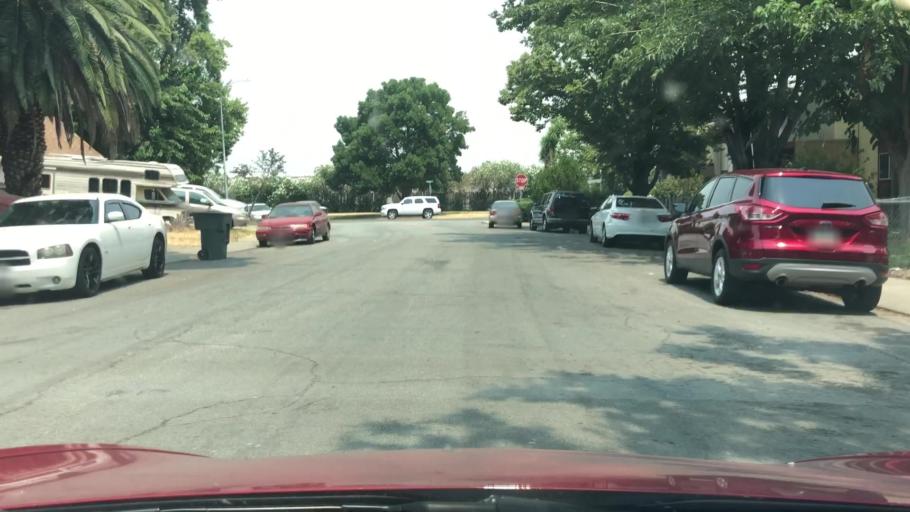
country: US
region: California
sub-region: San Joaquin County
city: Tracy
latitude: 37.7373
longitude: -121.4411
